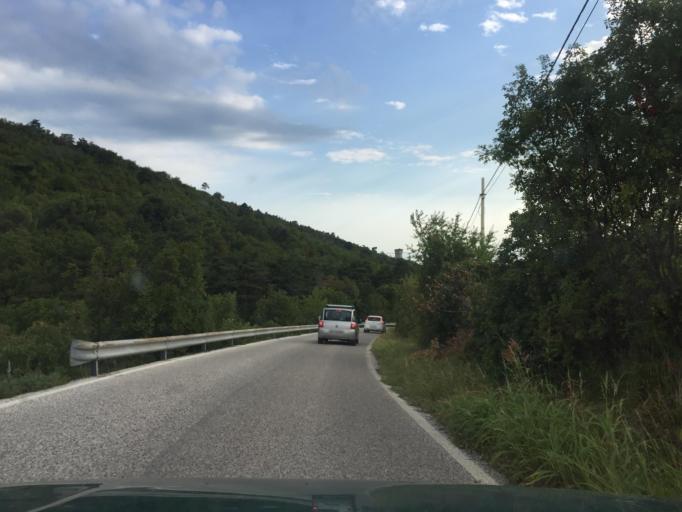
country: IT
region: Friuli Venezia Giulia
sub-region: Provincia di Trieste
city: Duino
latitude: 45.7938
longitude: 13.6013
